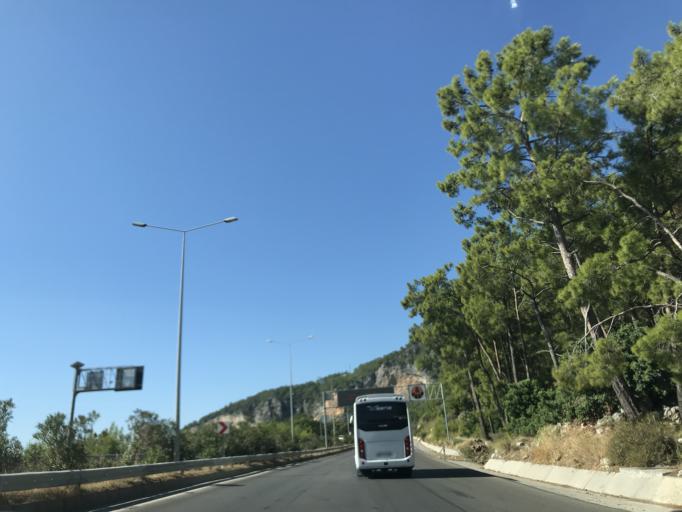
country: TR
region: Antalya
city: Cakirlar
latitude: 36.7581
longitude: 30.5695
